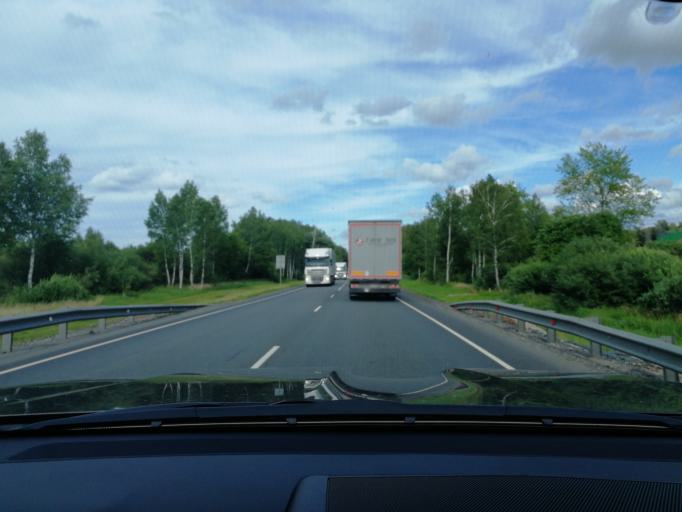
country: RU
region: Moskovskaya
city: Mikhnevo
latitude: 55.0745
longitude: 37.9112
